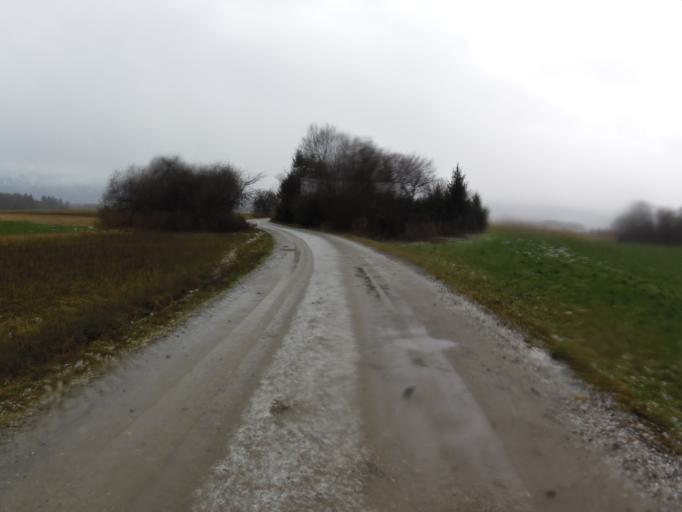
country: DE
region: Bavaria
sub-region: Upper Bavaria
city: Benediktbeuern
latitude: 47.6976
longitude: 11.3939
